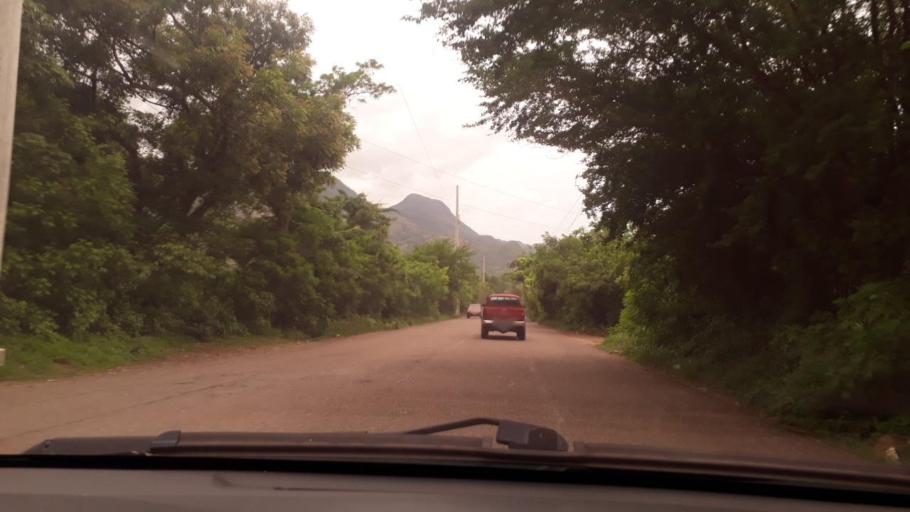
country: GT
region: Chiquimula
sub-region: Municipio de Jocotan
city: Jocotan
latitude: 14.7989
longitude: -89.3943
